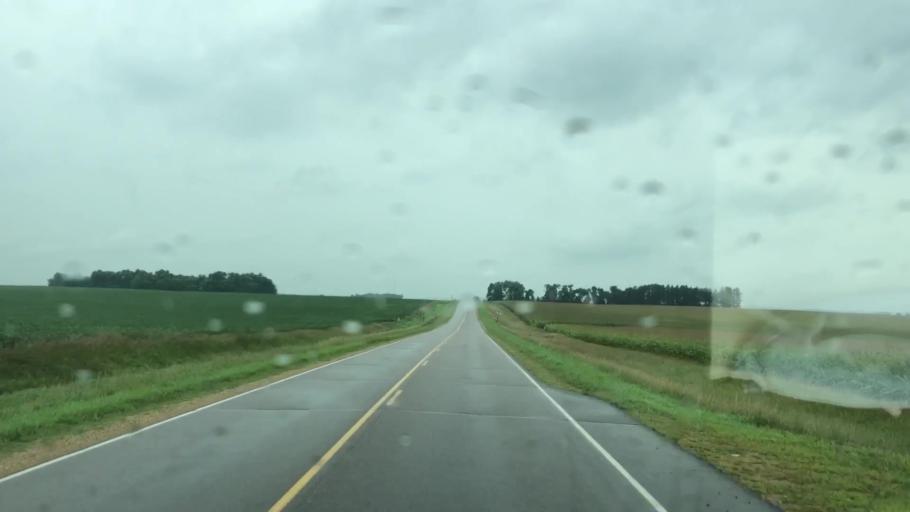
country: US
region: Iowa
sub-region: O'Brien County
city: Sanborn
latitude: 43.2224
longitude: -95.7234
